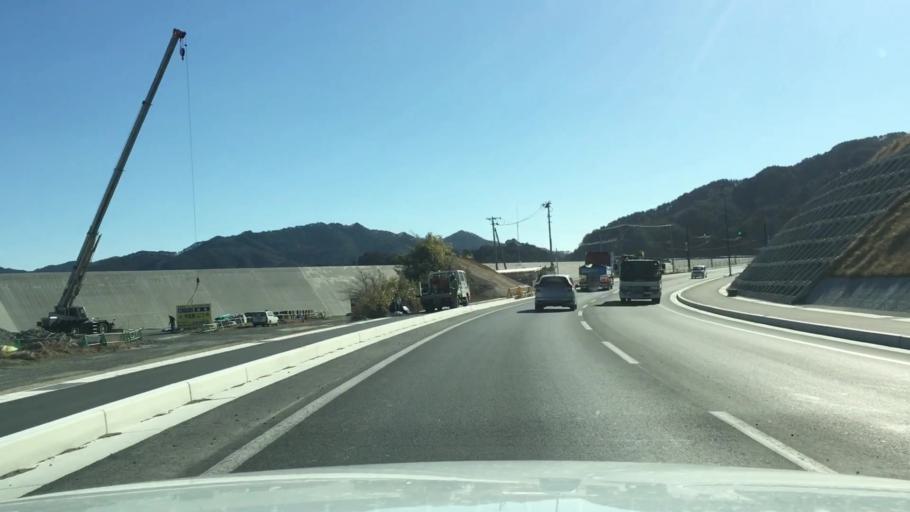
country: JP
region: Iwate
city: Yamada
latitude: 39.4547
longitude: 141.9600
